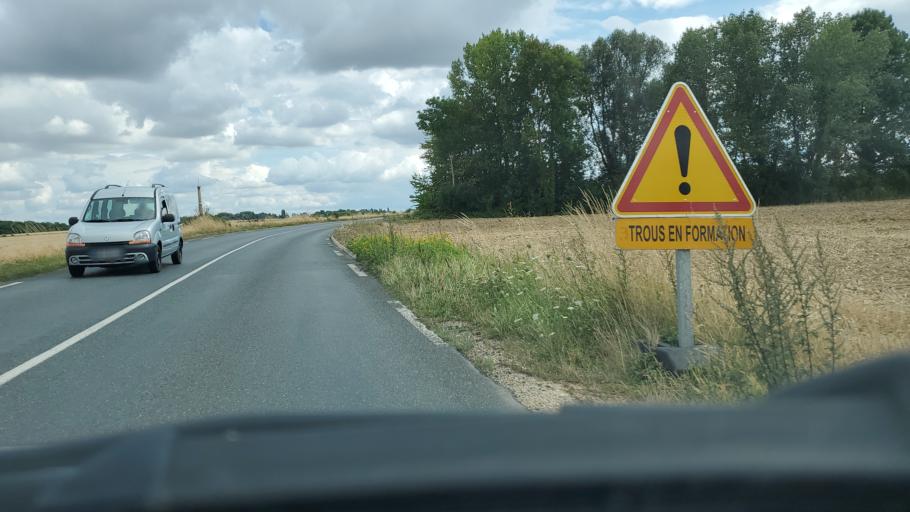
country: FR
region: Ile-de-France
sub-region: Departement de Seine-et-Marne
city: Fublaines
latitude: 48.9075
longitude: 2.9276
